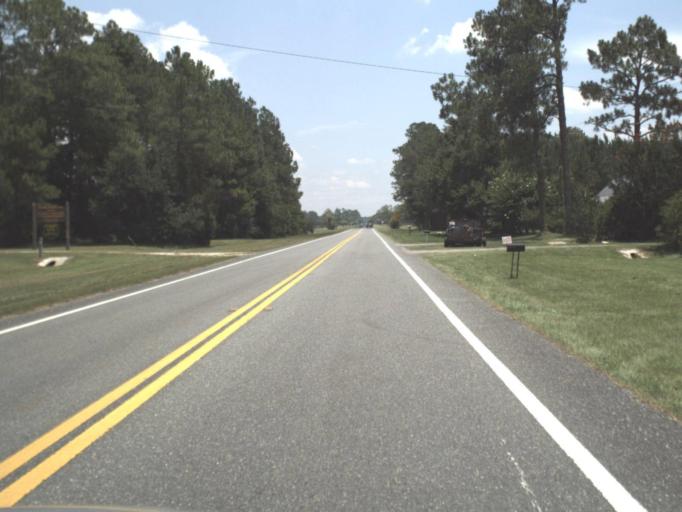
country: US
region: Florida
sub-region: Union County
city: Lake Butler
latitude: 30.0701
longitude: -82.2190
